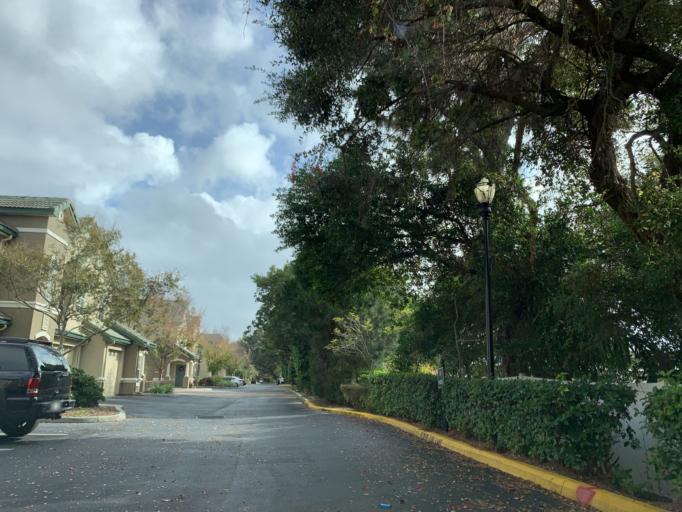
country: US
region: Florida
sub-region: Pinellas County
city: South Highpoint
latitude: 27.9532
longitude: -82.7281
